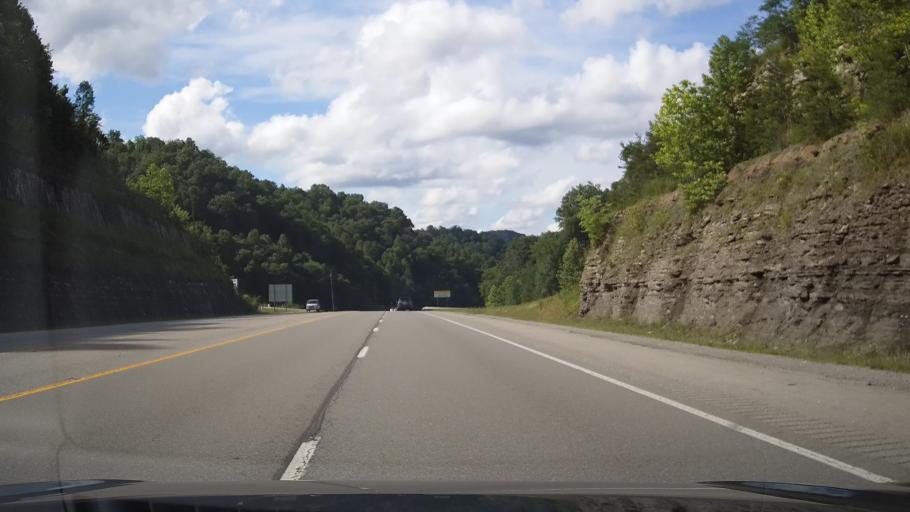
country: US
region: Kentucky
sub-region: Floyd County
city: Prestonsburg
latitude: 37.6697
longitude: -82.7933
